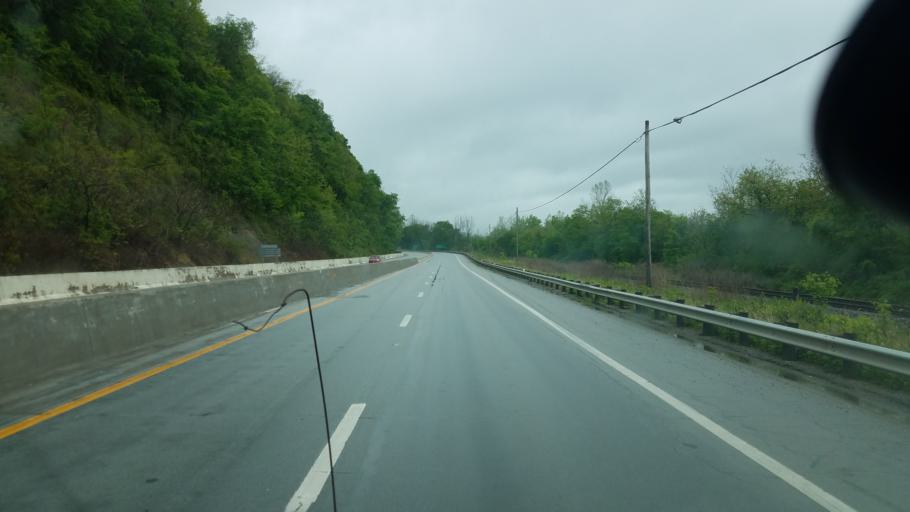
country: US
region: Ohio
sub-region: Belmont County
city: Martins Ferry
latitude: 40.1186
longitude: -80.7099
